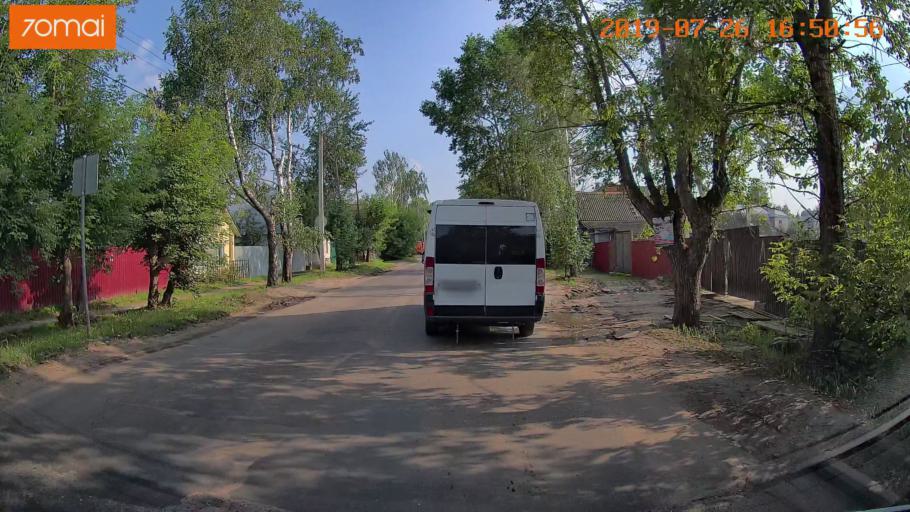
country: RU
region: Ivanovo
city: Bogorodskoye
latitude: 57.0217
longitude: 41.0207
